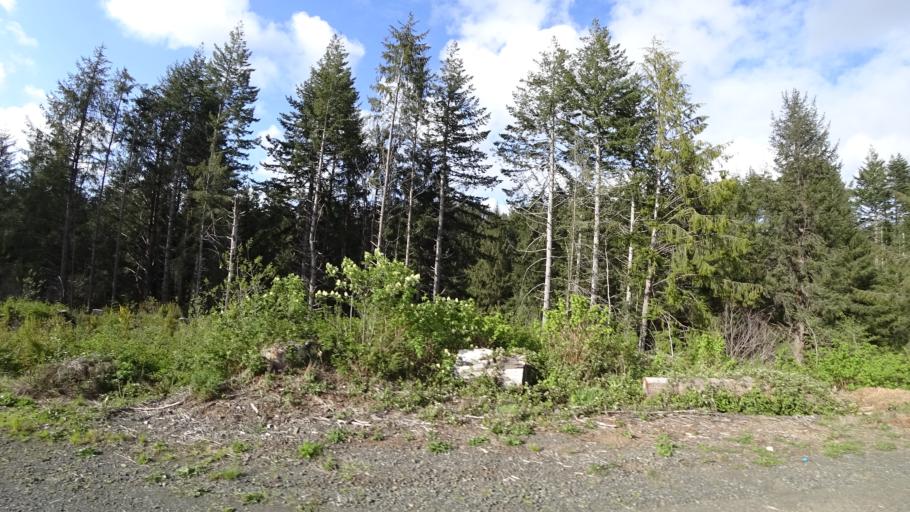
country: US
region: Oregon
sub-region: Douglas County
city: Reedsport
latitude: 43.7578
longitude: -124.1314
